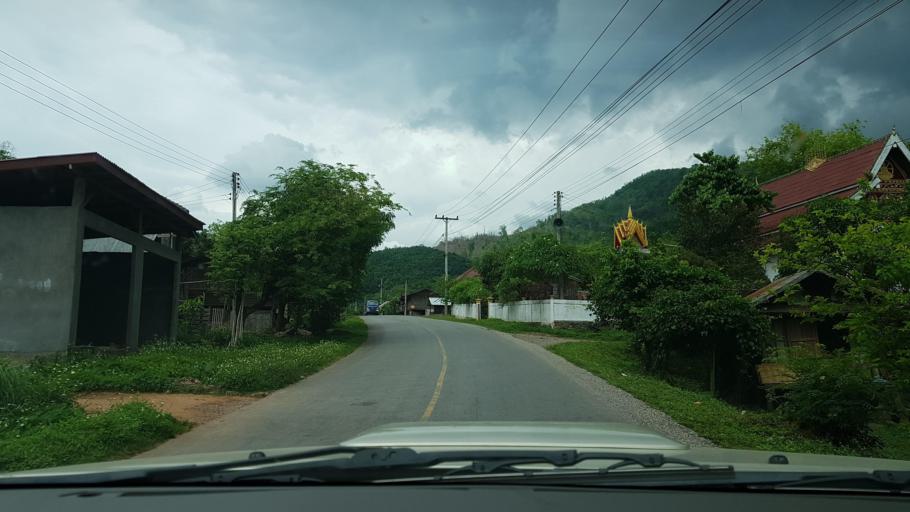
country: LA
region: Loungnamtha
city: Muang Nale
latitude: 20.3579
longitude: 101.7077
